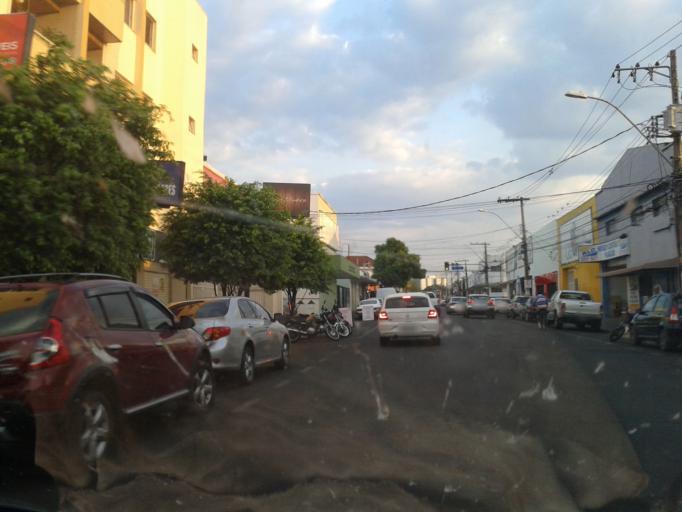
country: BR
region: Minas Gerais
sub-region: Uberlandia
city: Uberlandia
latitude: -18.9082
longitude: -48.2780
